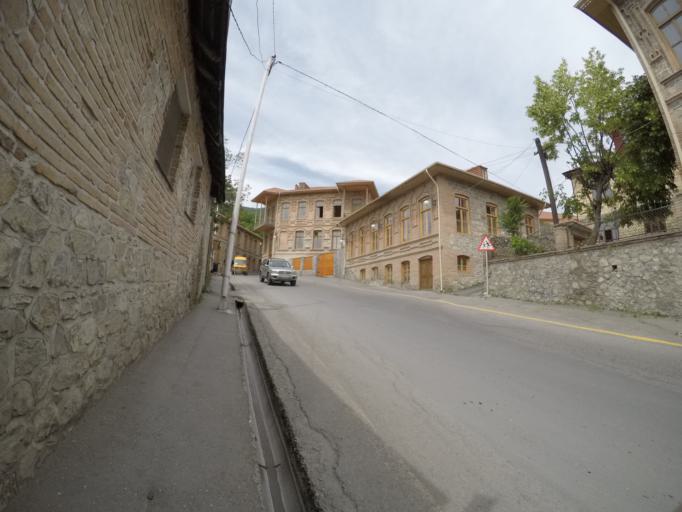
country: AZ
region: Shaki City
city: Sheki
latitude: 41.2013
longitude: 47.1949
